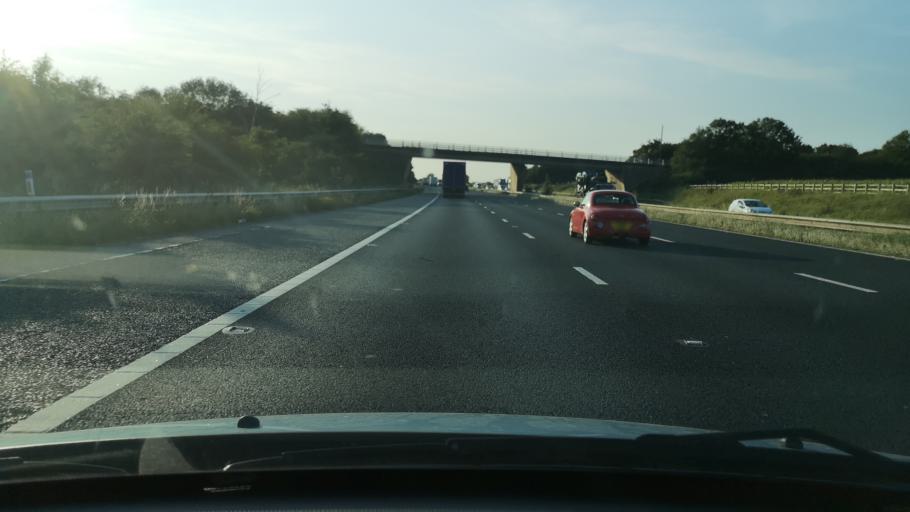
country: GB
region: England
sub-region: East Riding of Yorkshire
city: Pollington
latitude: 53.6930
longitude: -1.1177
